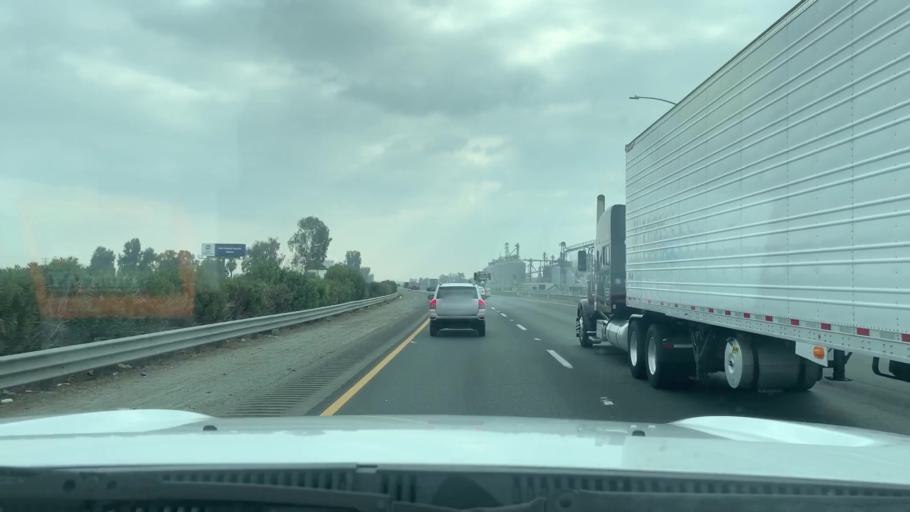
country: US
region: California
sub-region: Tulare County
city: Pixley
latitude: 36.0038
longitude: -119.3016
